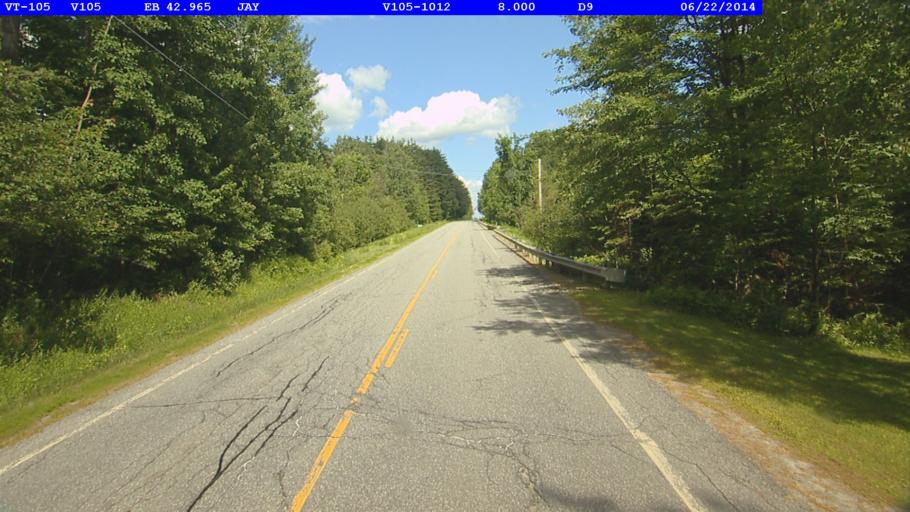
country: US
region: Vermont
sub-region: Orleans County
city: Newport
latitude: 44.9645
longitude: -72.4298
